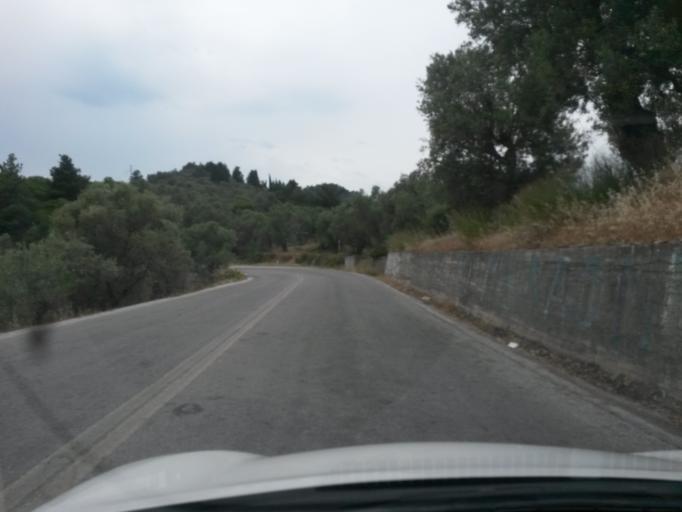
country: GR
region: North Aegean
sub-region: Nomos Lesvou
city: Skopelos
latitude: 39.0174
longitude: 26.4657
